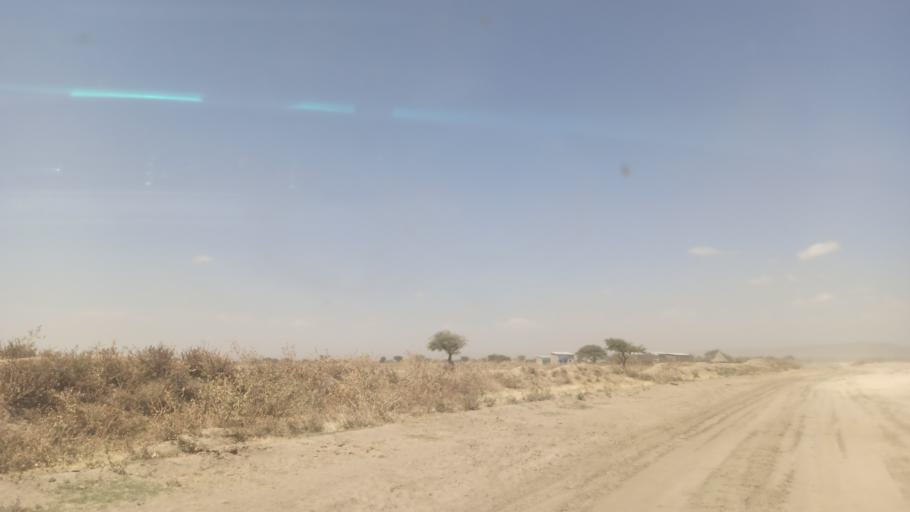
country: ET
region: Oromiya
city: Ziway
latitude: 7.7367
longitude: 38.6219
